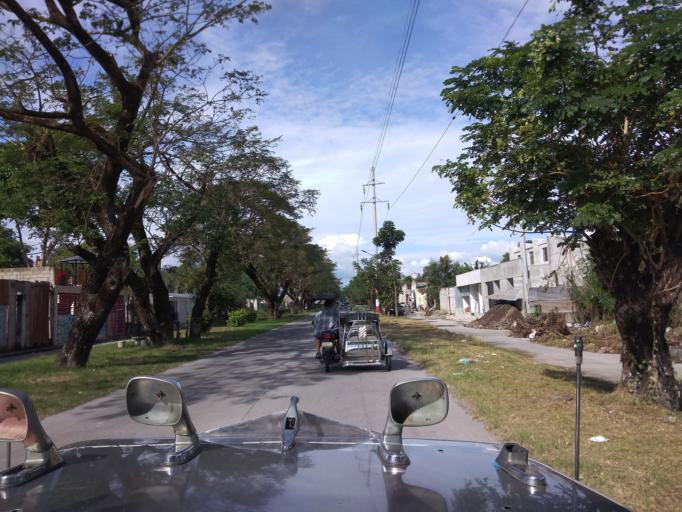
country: PH
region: Central Luzon
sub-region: Province of Pampanga
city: Pandacaqui
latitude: 15.1780
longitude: 120.6574
